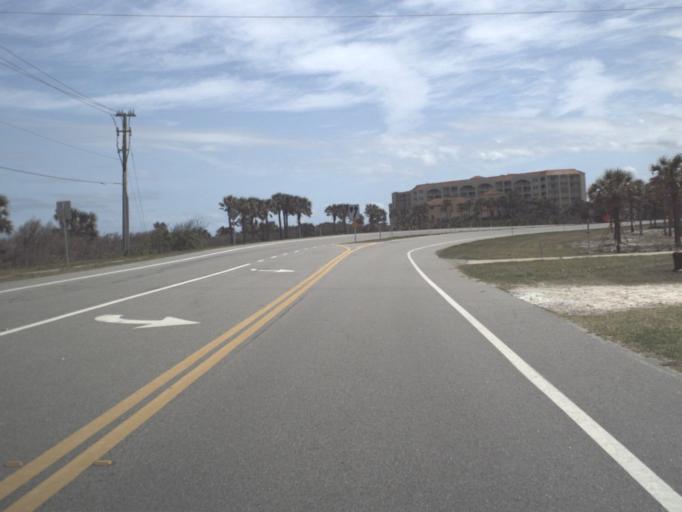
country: US
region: Florida
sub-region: Flagler County
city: Palm Coast
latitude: 29.6543
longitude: -81.2072
